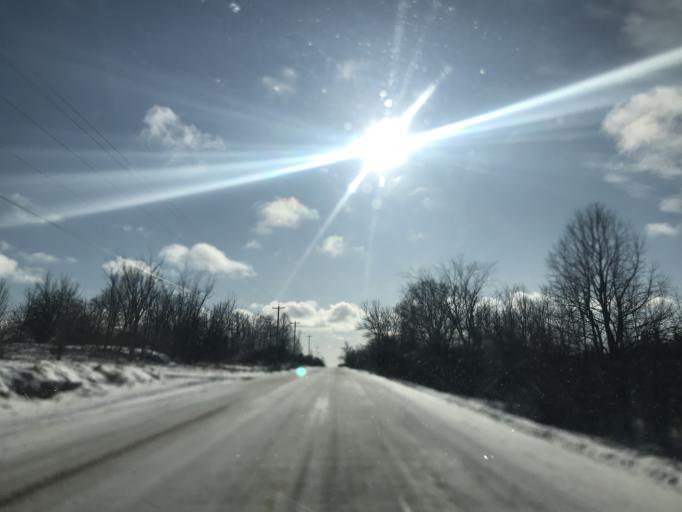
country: US
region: Wisconsin
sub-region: Kewaunee County
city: Luxemburg
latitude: 44.7064
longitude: -87.6207
